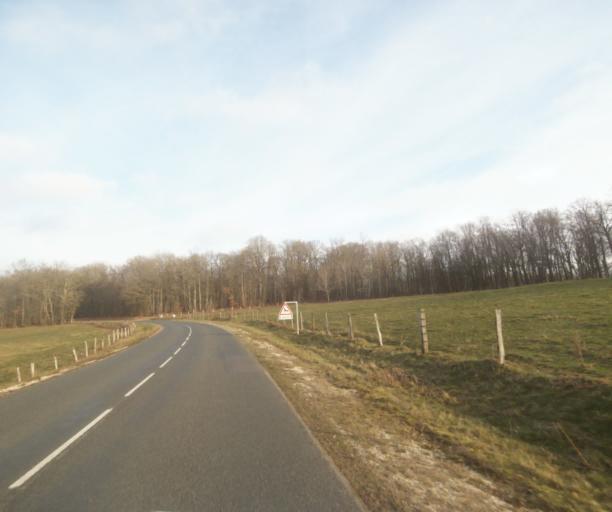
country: FR
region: Champagne-Ardenne
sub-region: Departement de la Marne
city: Sermaize-les-Bains
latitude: 48.7485
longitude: 4.9043
